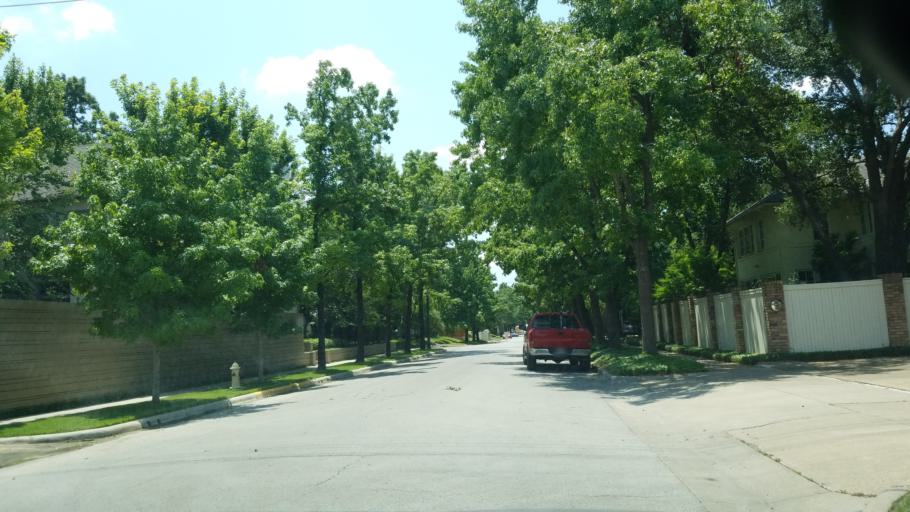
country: US
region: Texas
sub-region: Dallas County
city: Highland Park
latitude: 32.8317
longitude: -96.7891
